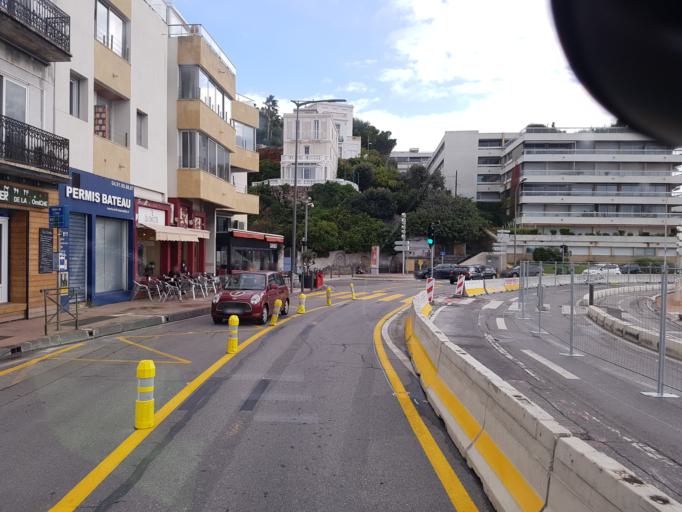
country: FR
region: Provence-Alpes-Cote d'Azur
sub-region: Departement des Bouches-du-Rhone
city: Marseille 07
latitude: 43.2756
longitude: 5.3596
